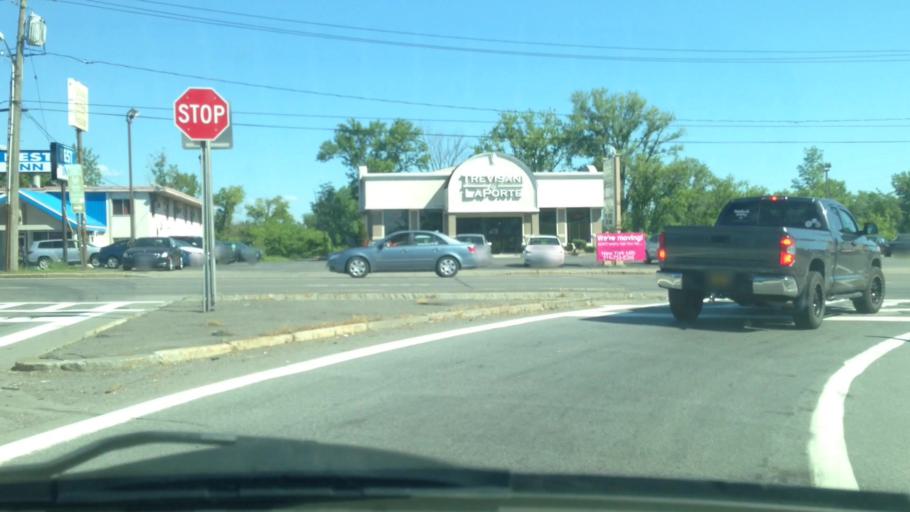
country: US
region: New York
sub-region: Oneida County
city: Utica
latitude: 43.1134
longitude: -75.2147
